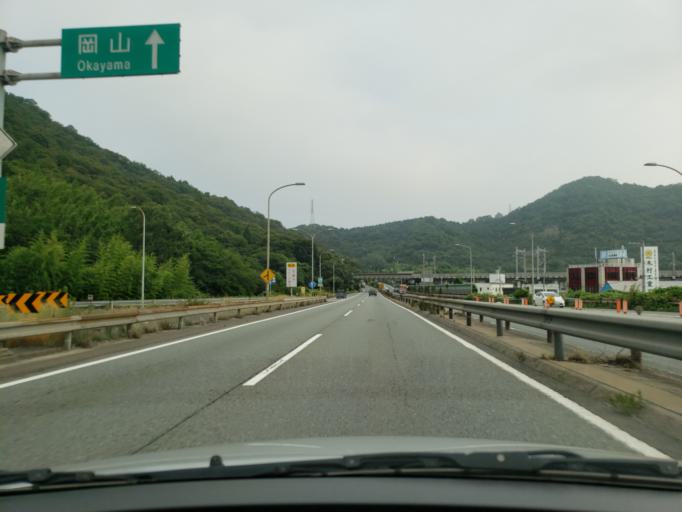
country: JP
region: Hyogo
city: Himeji
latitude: 34.8291
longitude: 134.6333
